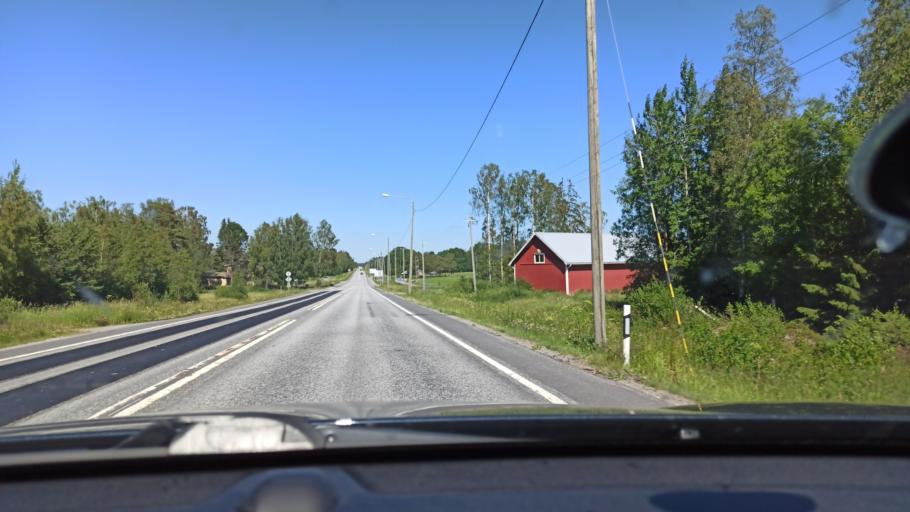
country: FI
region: Ostrobothnia
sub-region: Vaasa
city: Voera
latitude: 63.2258
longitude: 22.2343
